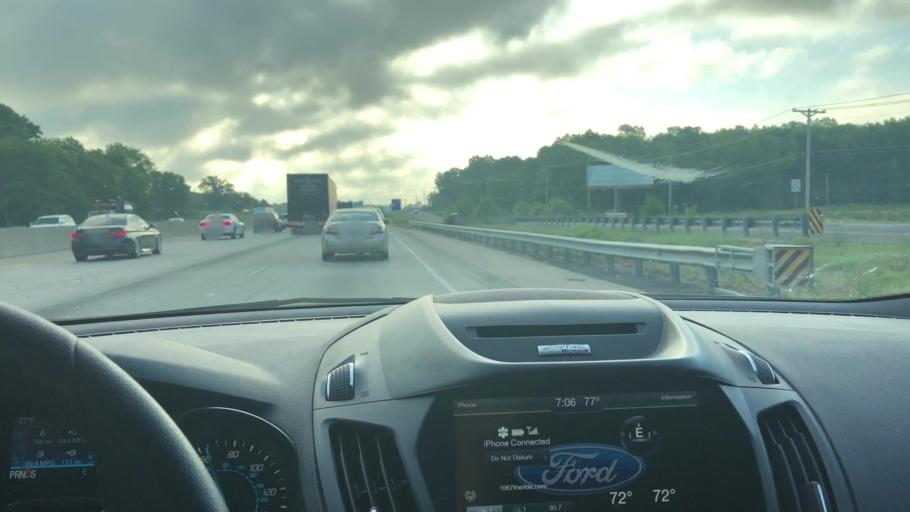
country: US
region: Arkansas
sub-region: Pulaski County
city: Alexander
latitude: 34.6466
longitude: -92.4265
